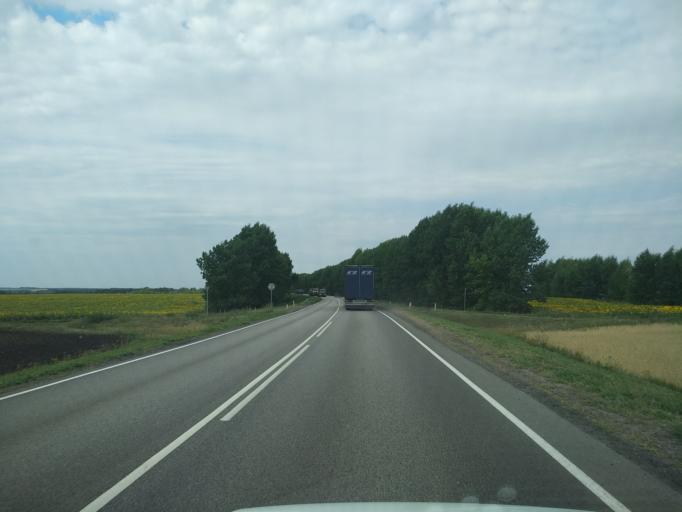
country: RU
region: Voronezj
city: Pereleshinskiy
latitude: 51.8494
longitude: 40.3166
